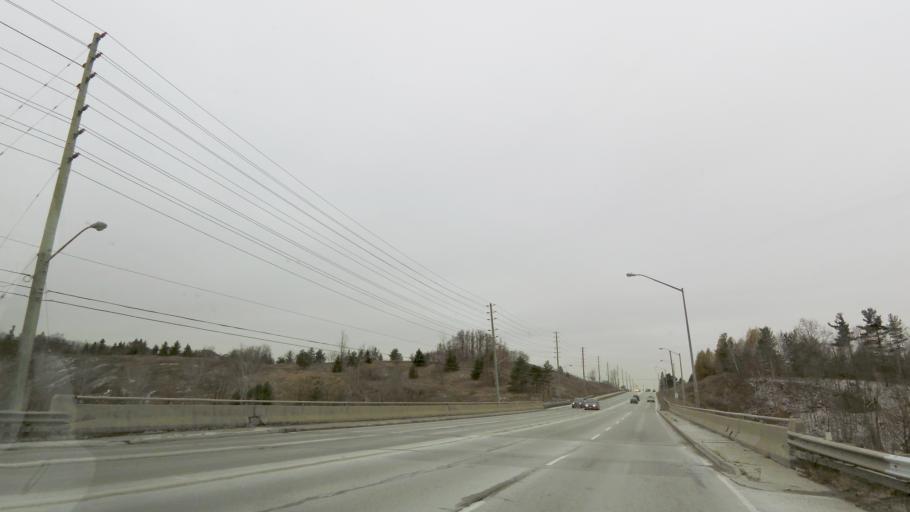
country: CA
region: Ontario
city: Vaughan
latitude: 43.8195
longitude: -79.5895
